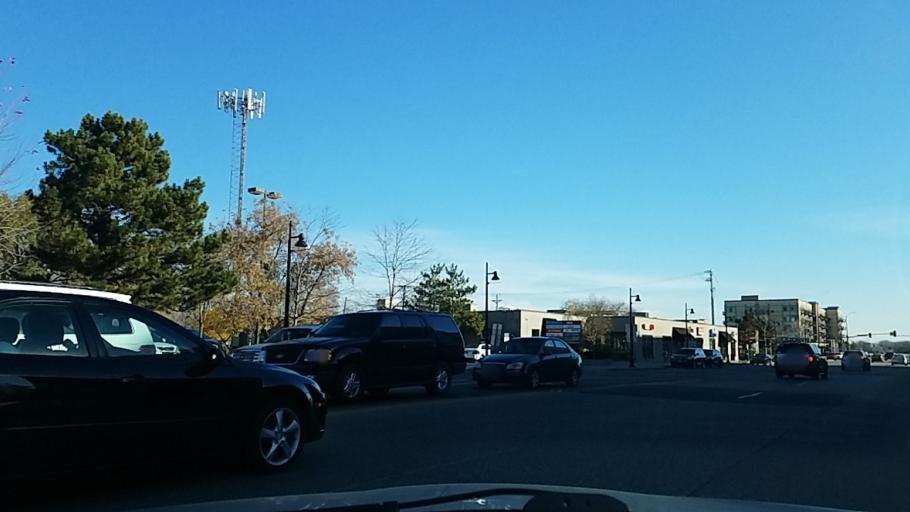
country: US
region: Minnesota
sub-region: Hennepin County
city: Saint Louis Park
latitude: 44.9377
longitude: -93.3546
